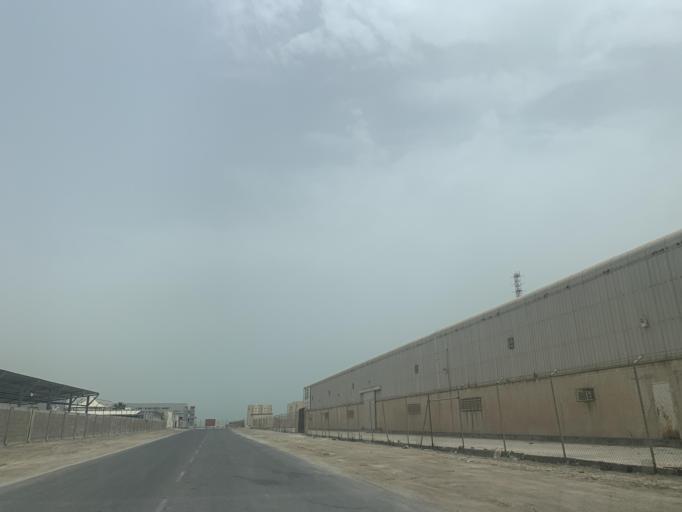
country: BH
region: Northern
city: Sitrah
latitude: 26.1775
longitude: 50.6239
